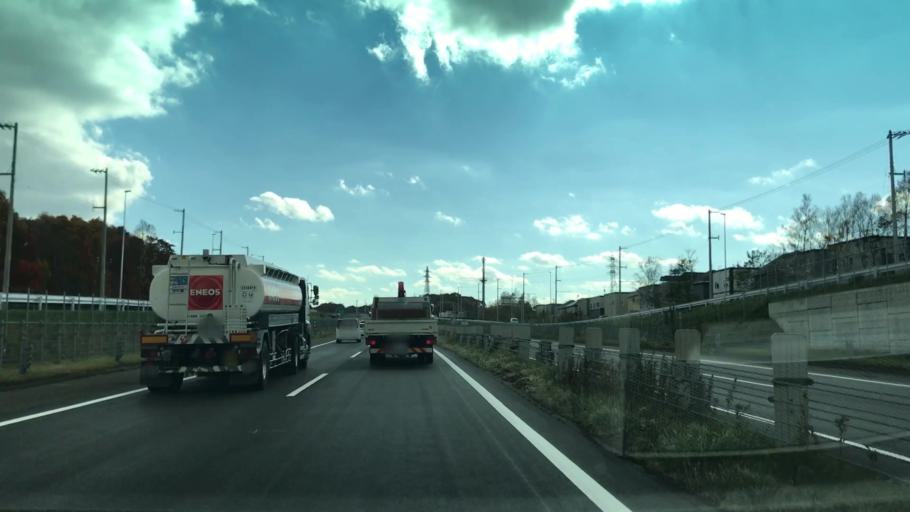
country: JP
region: Hokkaido
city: Kitahiroshima
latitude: 42.9898
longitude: 141.4700
